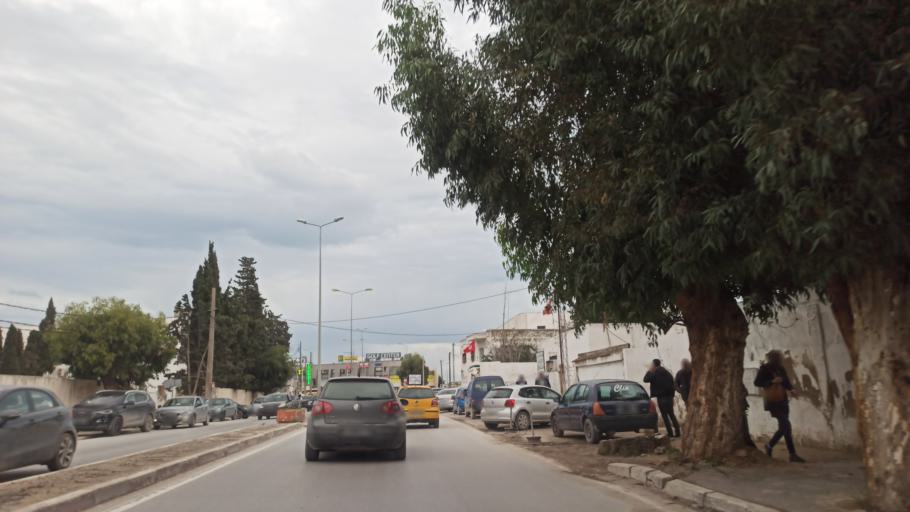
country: TN
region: Ariana
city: Ariana
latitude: 36.8748
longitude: 10.2432
